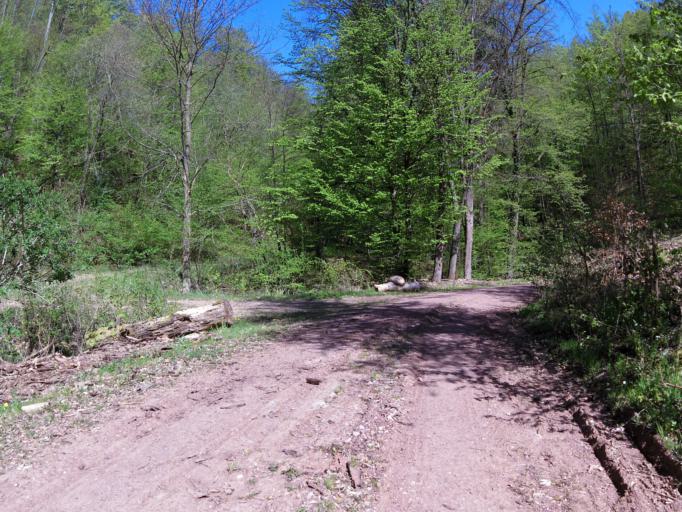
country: DE
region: Thuringia
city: Wolfsburg-Unkeroda
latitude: 50.9701
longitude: 10.2658
